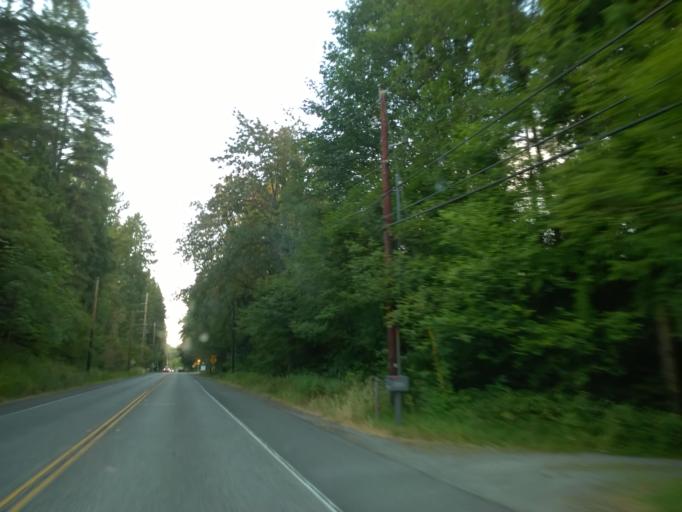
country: US
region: Washington
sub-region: King County
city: Cottage Lake
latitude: 47.7322
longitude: -122.0822
